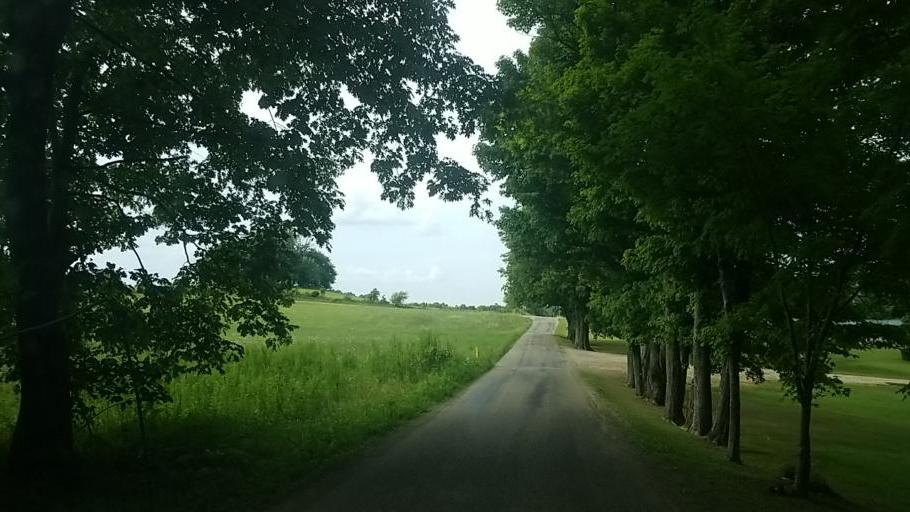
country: US
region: Ohio
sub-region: Richland County
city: Lexington
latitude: 40.6286
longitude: -82.5779
